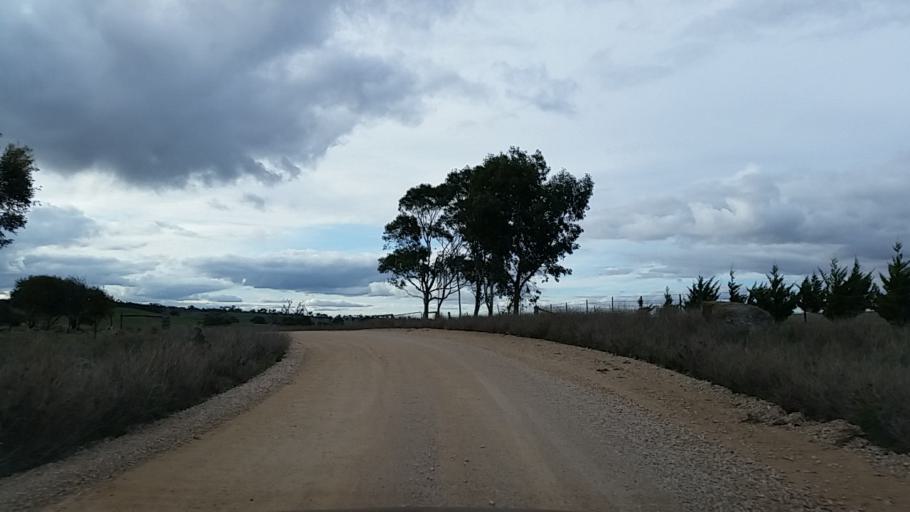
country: AU
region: South Australia
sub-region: Mount Barker
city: Callington
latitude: -34.9775
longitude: 139.0582
